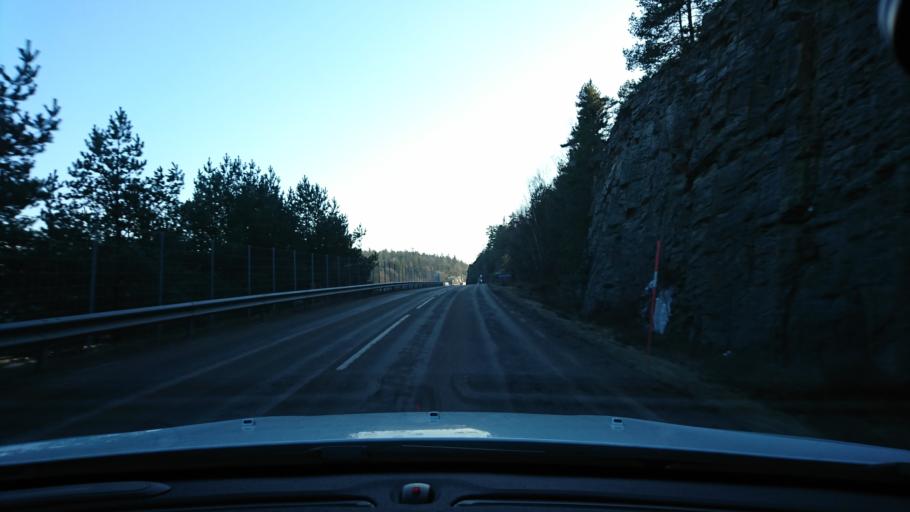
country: SE
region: Vaestra Goetaland
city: Svanesund
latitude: 58.1552
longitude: 11.8867
